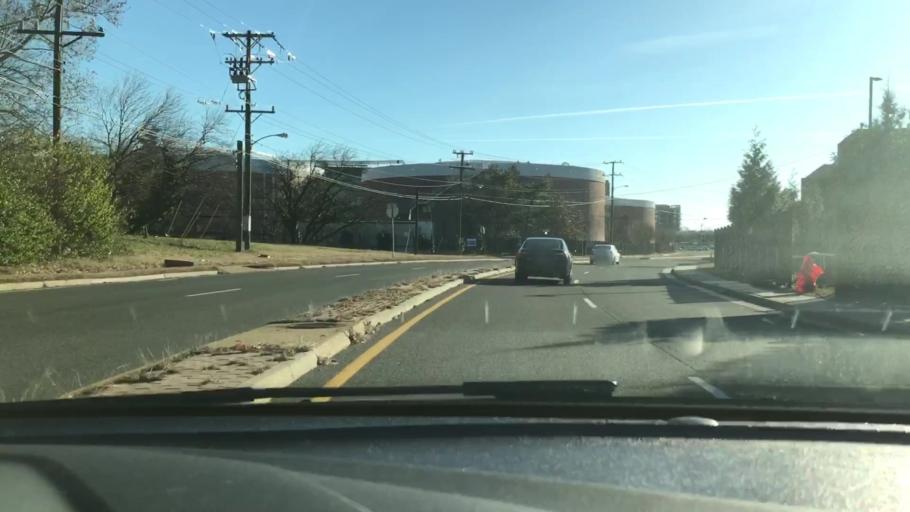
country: US
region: Virginia
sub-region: City of Alexandria
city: Alexandria
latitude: 38.8442
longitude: -77.0577
